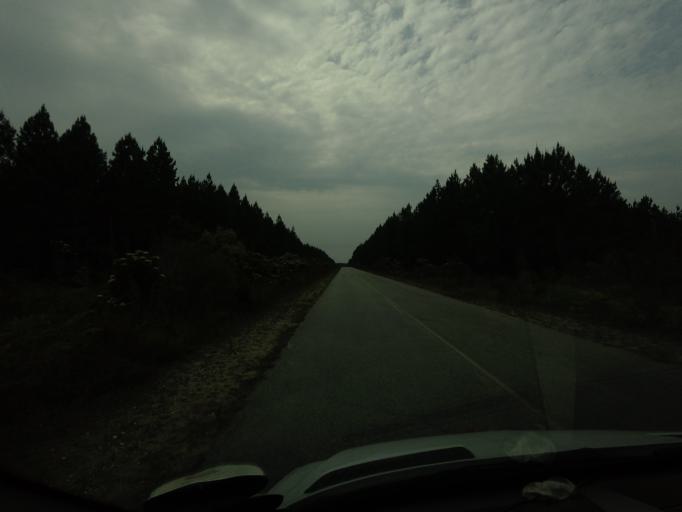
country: ZA
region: Eastern Cape
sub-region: Cacadu District Municipality
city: Kareedouw
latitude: -33.9917
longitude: 23.8438
